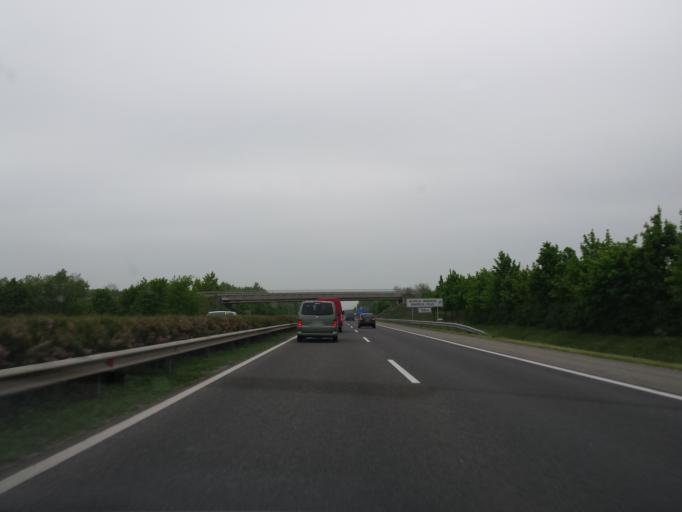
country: HU
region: Gyor-Moson-Sopron
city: Mosonszentmiklos
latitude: 47.7427
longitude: 17.4290
